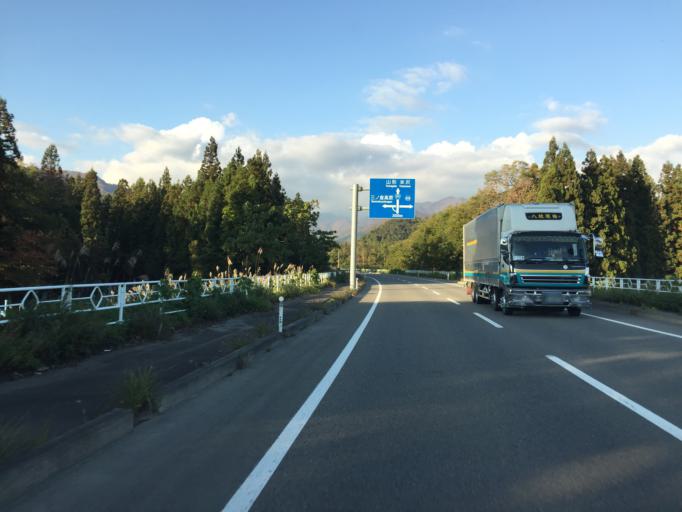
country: JP
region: Fukushima
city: Kitakata
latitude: 37.7247
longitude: 139.8724
